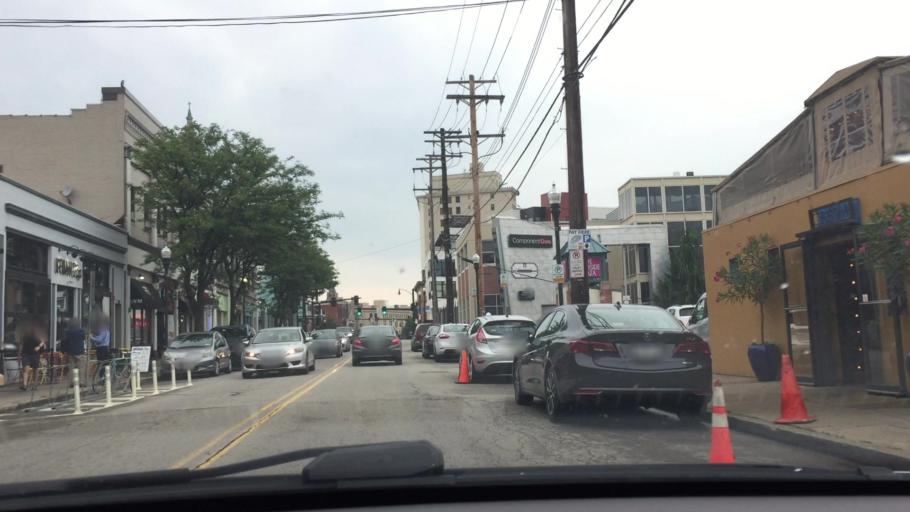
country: US
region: Pennsylvania
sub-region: Allegheny County
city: Bloomfield
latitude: 40.4581
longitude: -79.9251
